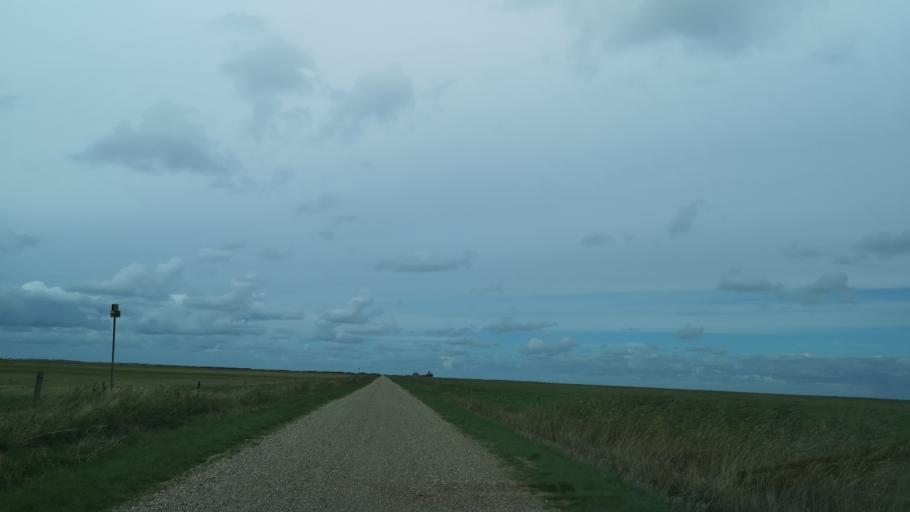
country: DK
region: Central Jutland
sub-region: Ringkobing-Skjern Kommune
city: Hvide Sande
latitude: 55.8816
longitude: 8.2223
